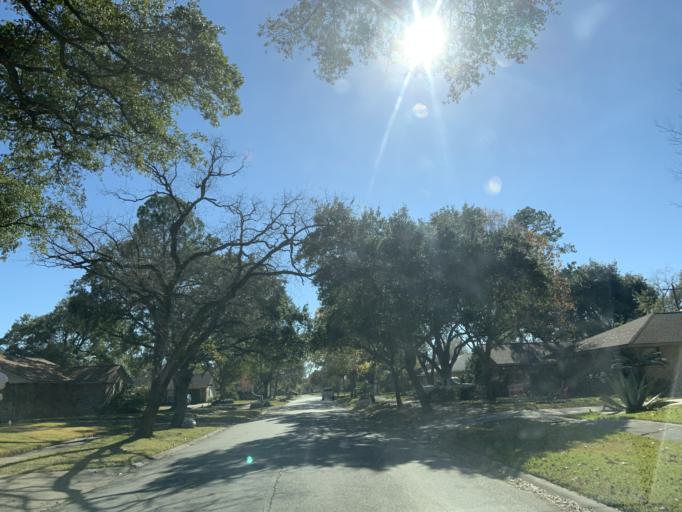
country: US
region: Texas
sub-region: Harris County
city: Bellaire
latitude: 29.6833
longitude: -95.5027
